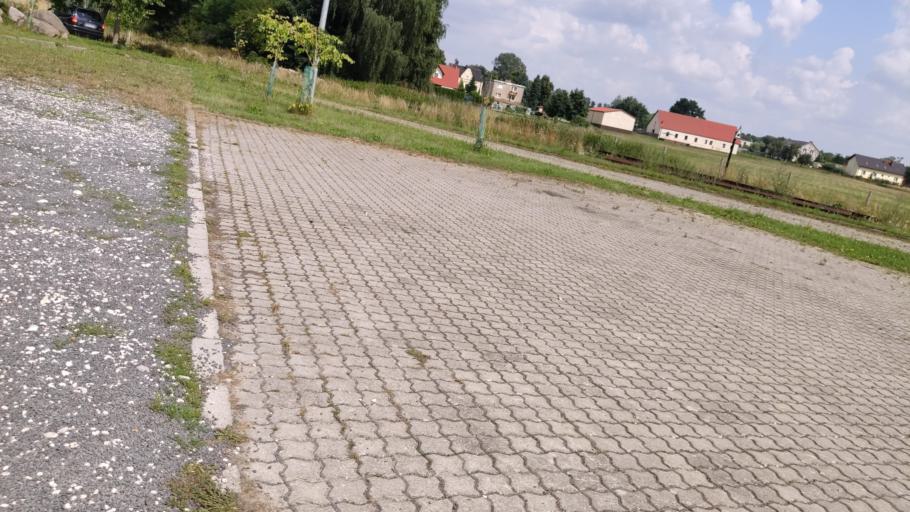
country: PL
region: Kujawsko-Pomorskie
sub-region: Powiat zninski
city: Gasawa
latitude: 52.7988
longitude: 17.7537
